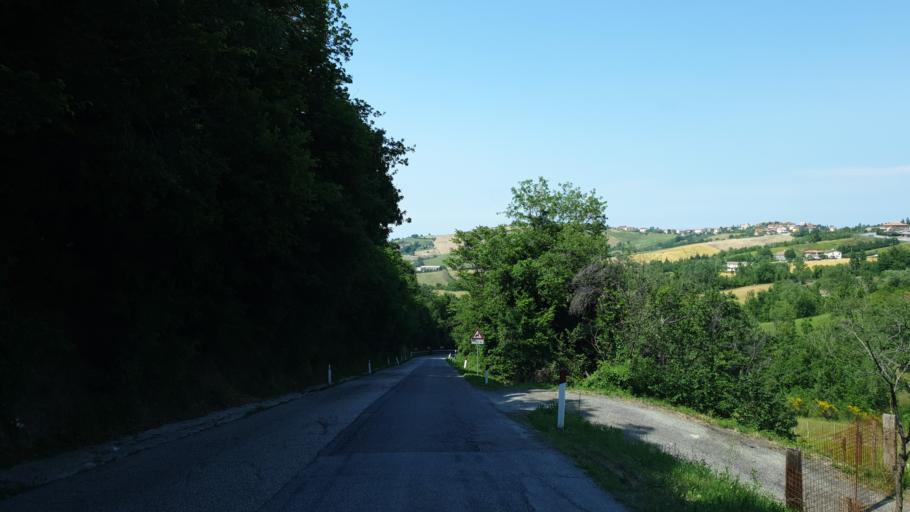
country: SM
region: San Marino
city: San Marino
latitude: 43.9393
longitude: 12.4328
